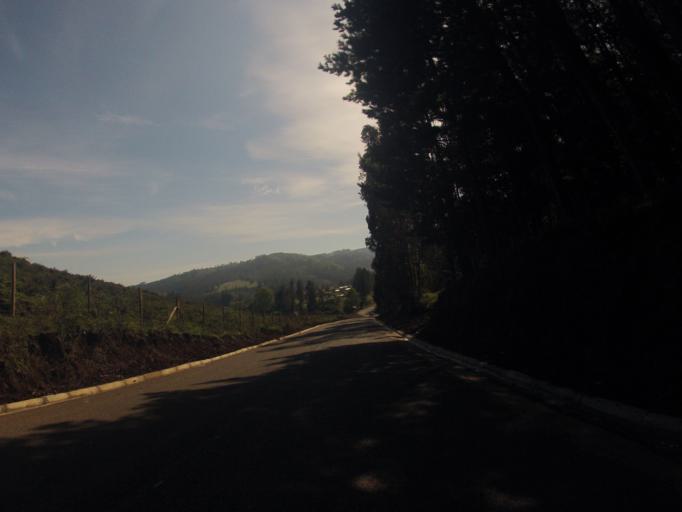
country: CL
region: Araucania
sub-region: Provincia de Cautin
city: Temuco
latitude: -38.6974
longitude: -72.5923
